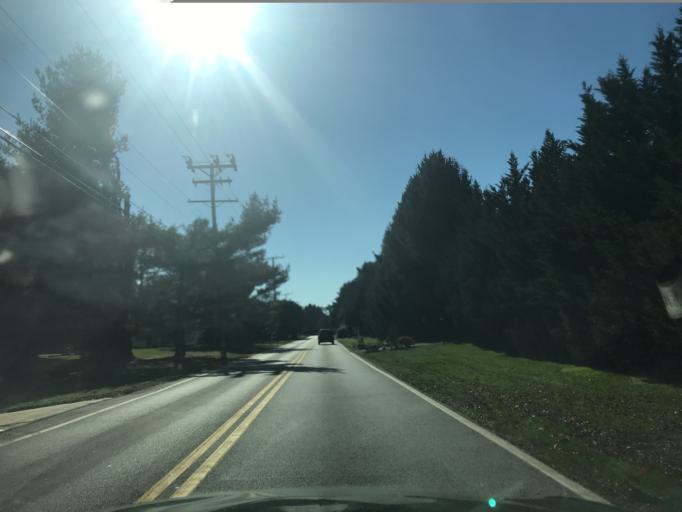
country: US
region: Maryland
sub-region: Baltimore County
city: Hampton
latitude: 39.5118
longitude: -76.5372
